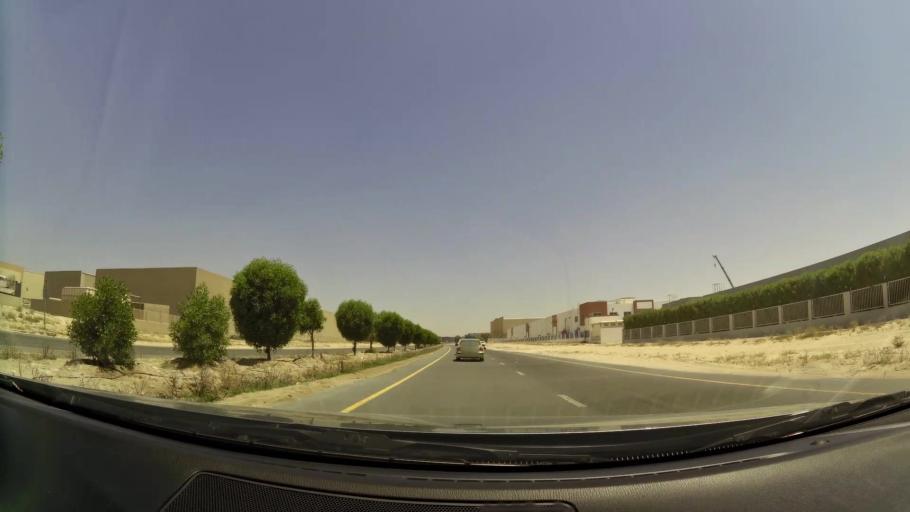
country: AE
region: Dubai
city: Dubai
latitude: 24.9672
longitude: 55.1979
